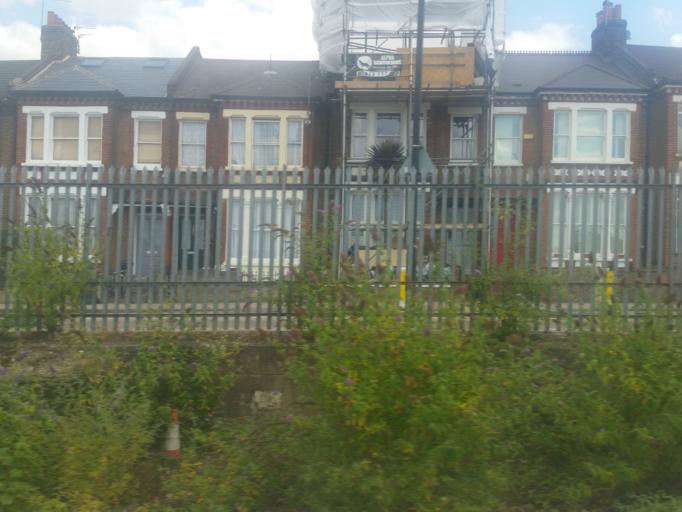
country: GB
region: England
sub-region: Greater London
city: Brixton
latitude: 51.4560
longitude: -0.1036
